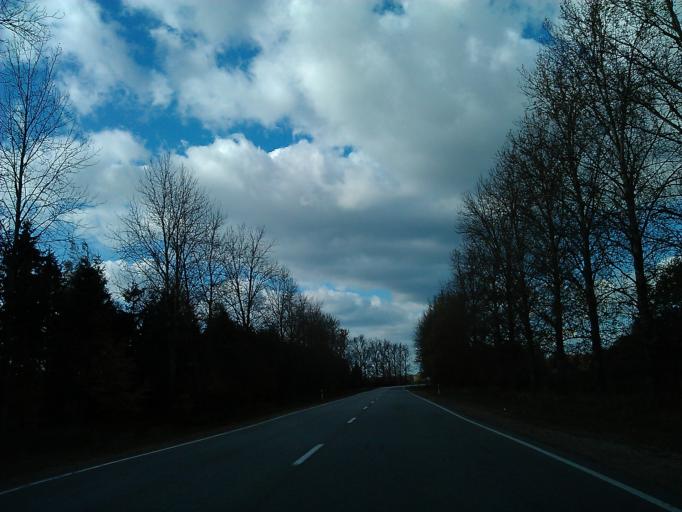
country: LV
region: Livani
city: Livani
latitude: 56.4114
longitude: 26.0906
